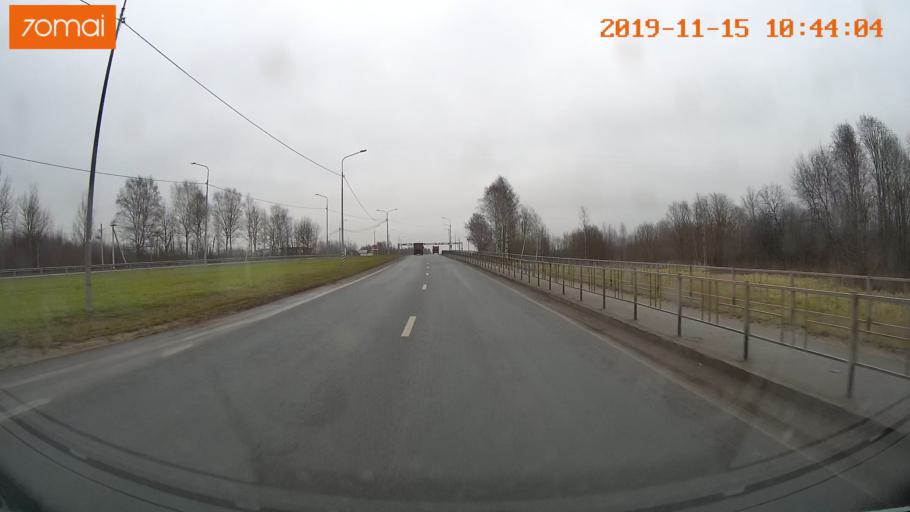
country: RU
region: Vologda
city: Sheksna
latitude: 59.2115
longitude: 38.5494
